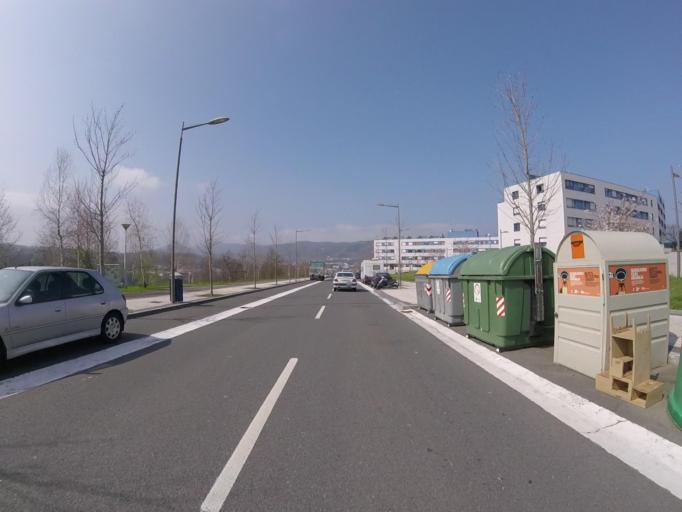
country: ES
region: Basque Country
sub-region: Provincia de Guipuzcoa
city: San Sebastian
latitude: 43.2991
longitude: -1.9944
